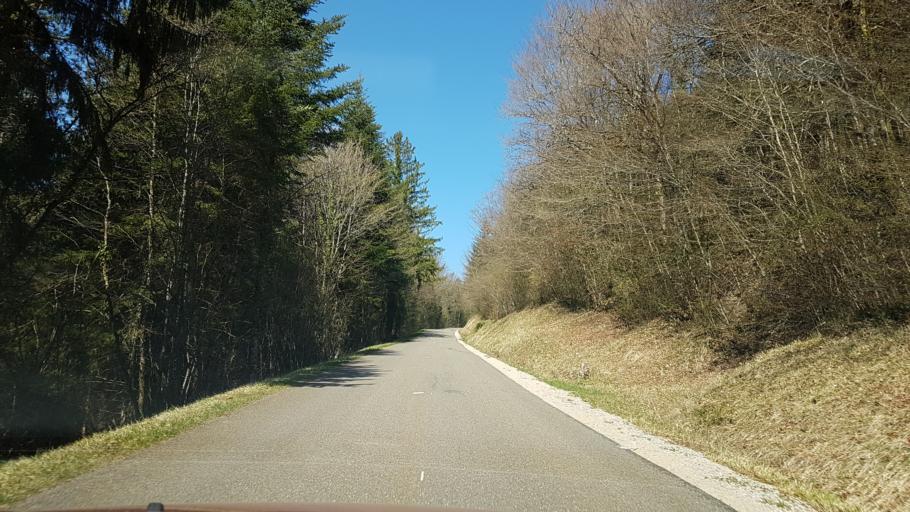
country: FR
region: Bourgogne
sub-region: Departement de Saone-et-Loire
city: Cuiseaux
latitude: 46.4827
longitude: 5.4801
